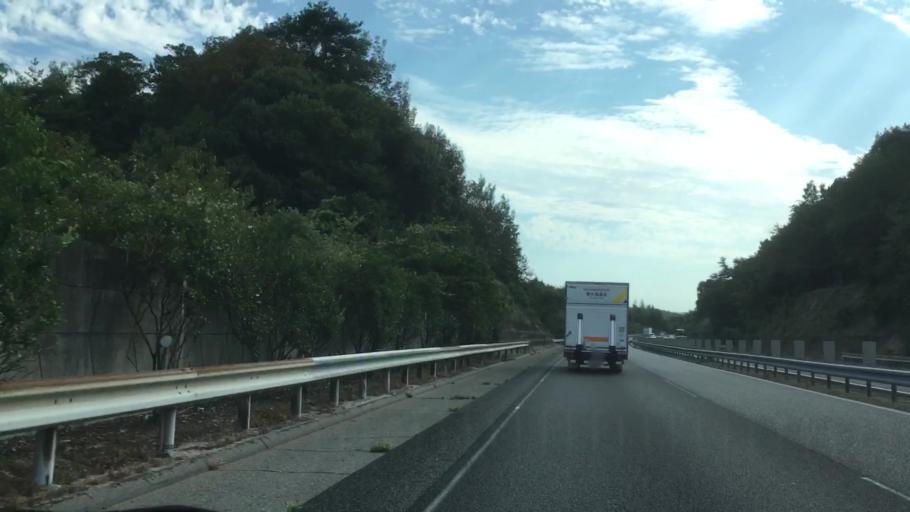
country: JP
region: Hiroshima
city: Ono-hara
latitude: 34.3106
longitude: 132.2803
